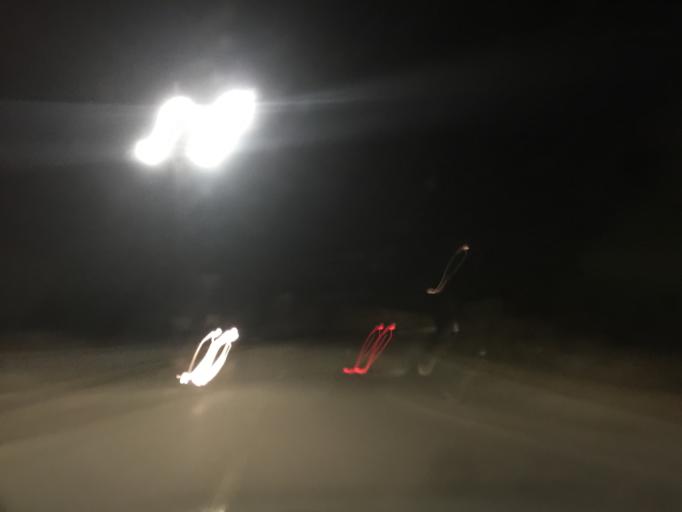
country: JO
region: Amman
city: Amman
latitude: 32.0195
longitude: 35.9598
